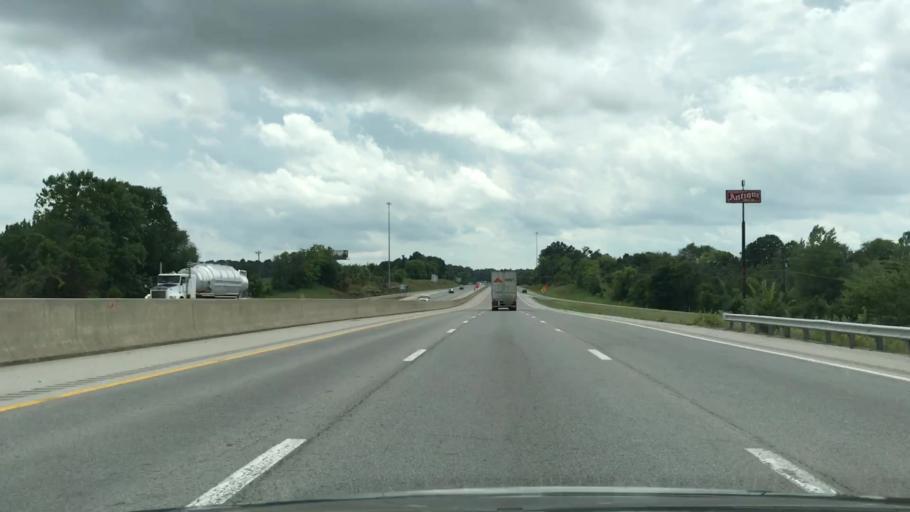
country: US
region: Kentucky
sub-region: Simpson County
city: Franklin
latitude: 36.6650
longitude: -86.5568
